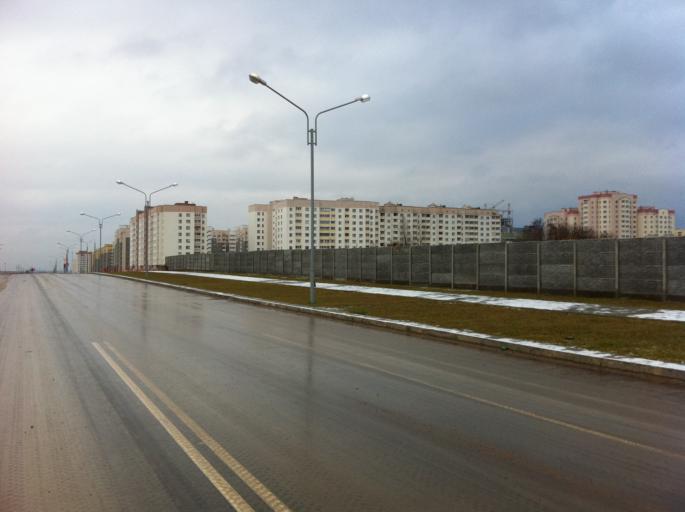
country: BY
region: Grodnenskaya
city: Hrodna
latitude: 53.7162
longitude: 23.8364
